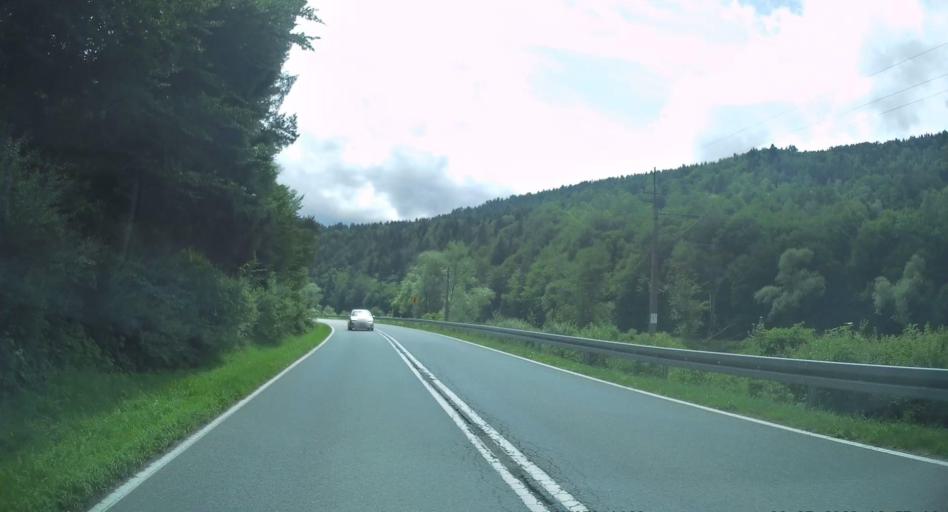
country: PL
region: Lesser Poland Voivodeship
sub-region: Powiat nowosadecki
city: Piwniczna-Zdroj
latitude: 49.3790
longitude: 20.7603
